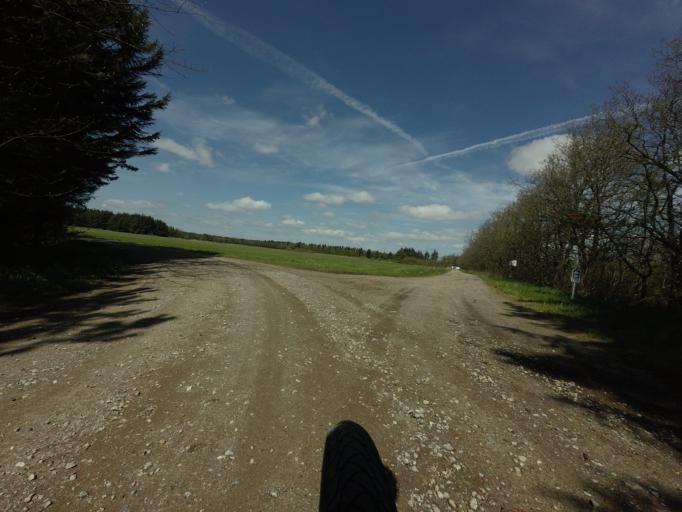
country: DK
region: North Denmark
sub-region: Jammerbugt Kommune
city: Brovst
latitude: 57.1561
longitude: 9.5621
